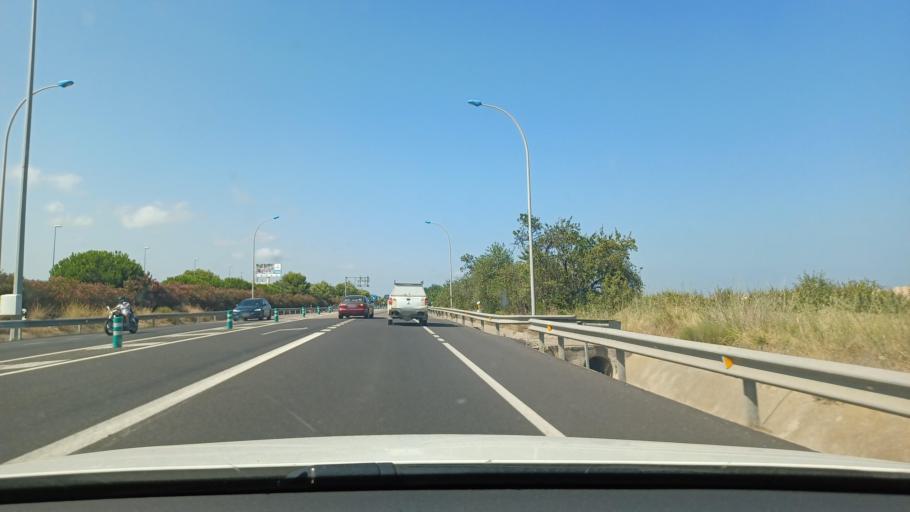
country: ES
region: Valencia
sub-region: Provincia de Castello
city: Orpesa/Oropesa del Mar
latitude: 40.1046
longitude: 0.1362
